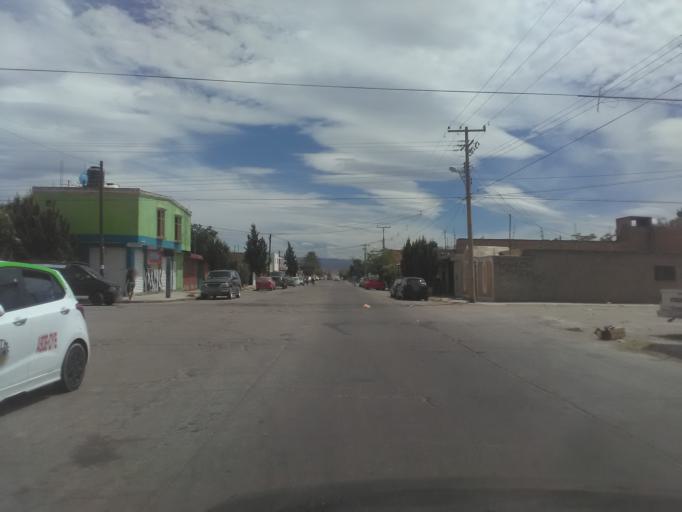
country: MX
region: Durango
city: Victoria de Durango
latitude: 24.0223
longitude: -104.6311
